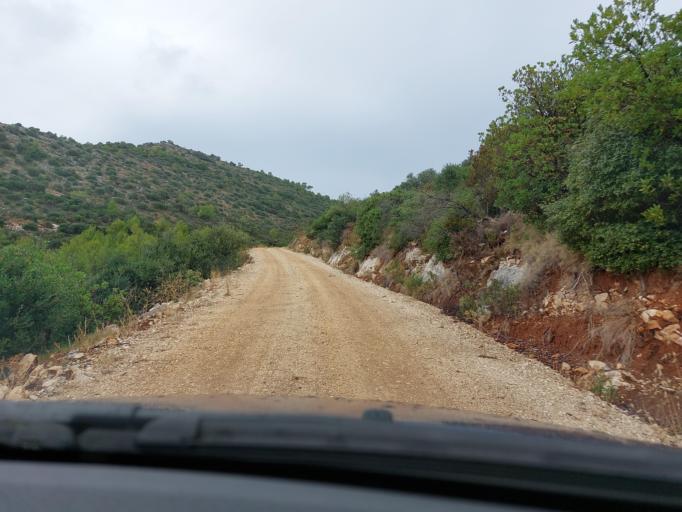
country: HR
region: Dubrovacko-Neretvanska
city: Smokvica
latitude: 42.7411
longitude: 16.9132
